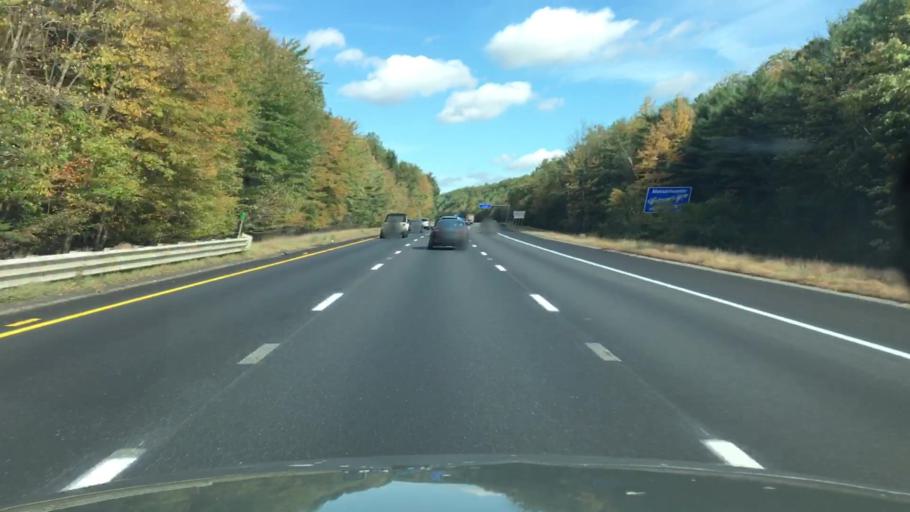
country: US
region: Massachusetts
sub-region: Hampden County
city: Holland
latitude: 42.0345
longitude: -72.1319
